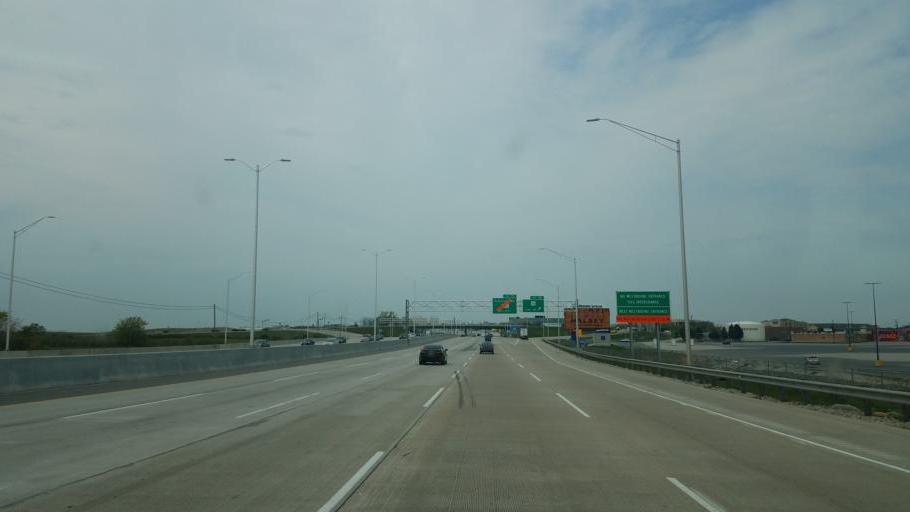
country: US
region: Illinois
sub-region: Cook County
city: Rosemont
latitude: 42.0030
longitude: -87.8883
